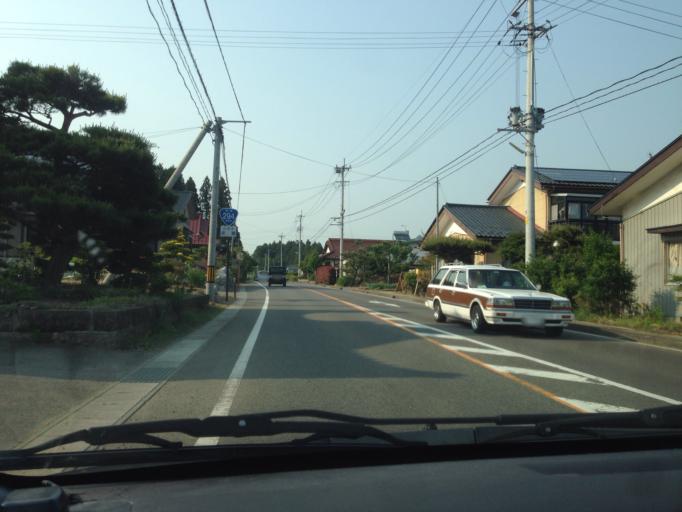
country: JP
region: Tochigi
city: Kuroiso
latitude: 37.0938
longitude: 140.1978
